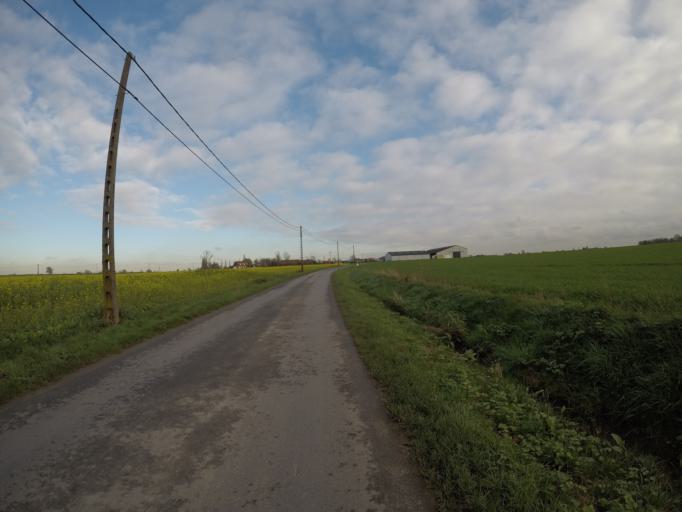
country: BE
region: Flanders
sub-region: Provincie West-Vlaanderen
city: Wervik
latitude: 50.8217
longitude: 3.0098
